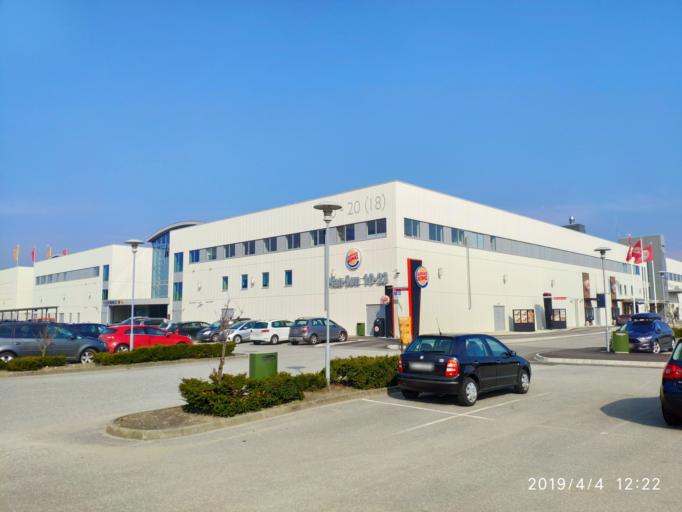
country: NO
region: Rogaland
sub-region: Klepp
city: Kleppe
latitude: 58.7782
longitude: 5.6268
